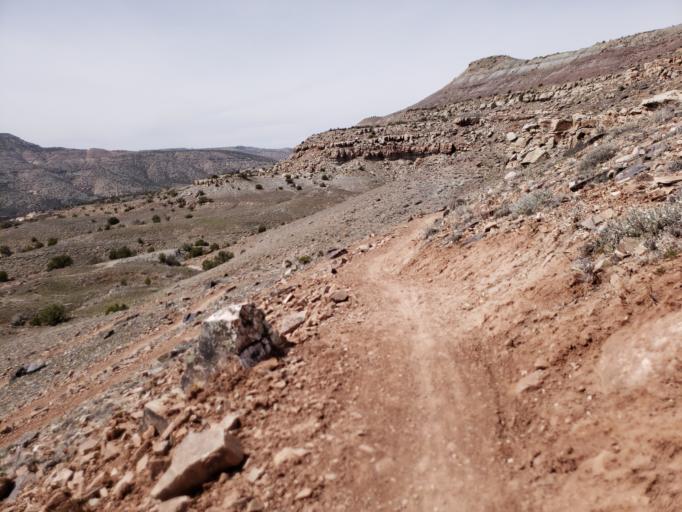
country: US
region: Colorado
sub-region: Mesa County
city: Loma
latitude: 39.1830
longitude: -108.8537
